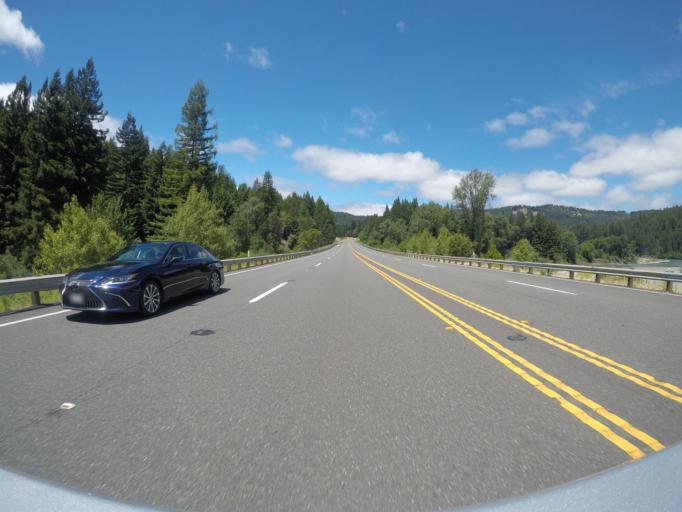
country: US
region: California
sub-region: Humboldt County
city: Redway
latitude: 40.2448
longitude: -123.8316
